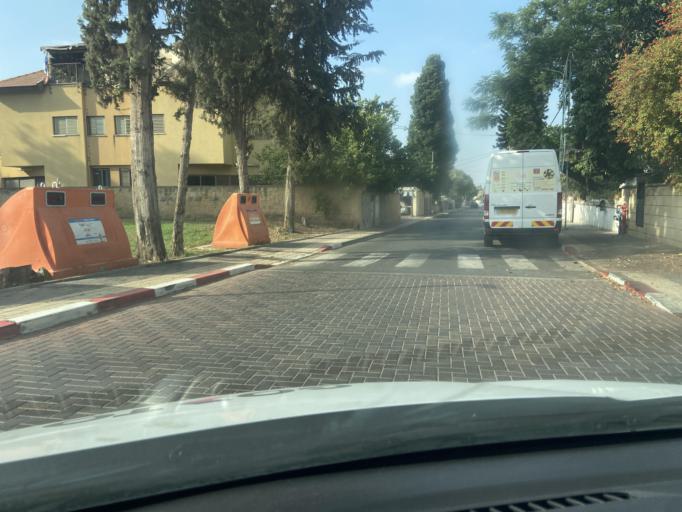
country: IL
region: Central District
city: Yehud
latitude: 32.0345
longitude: 34.8838
